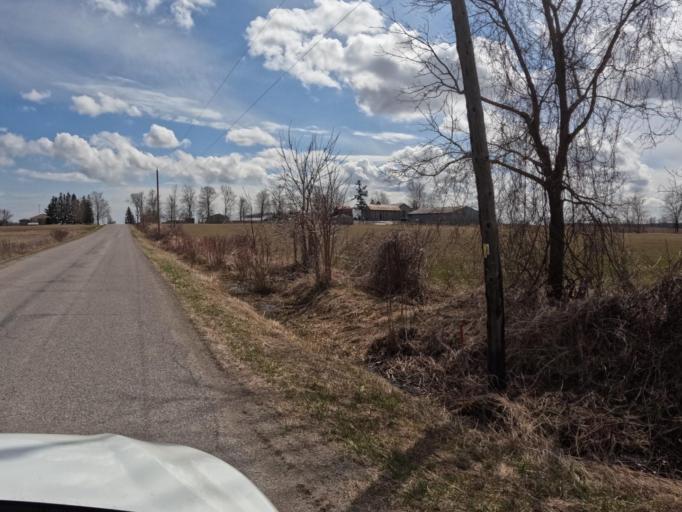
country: CA
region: Ontario
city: Norfolk County
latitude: 42.9296
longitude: -80.2010
